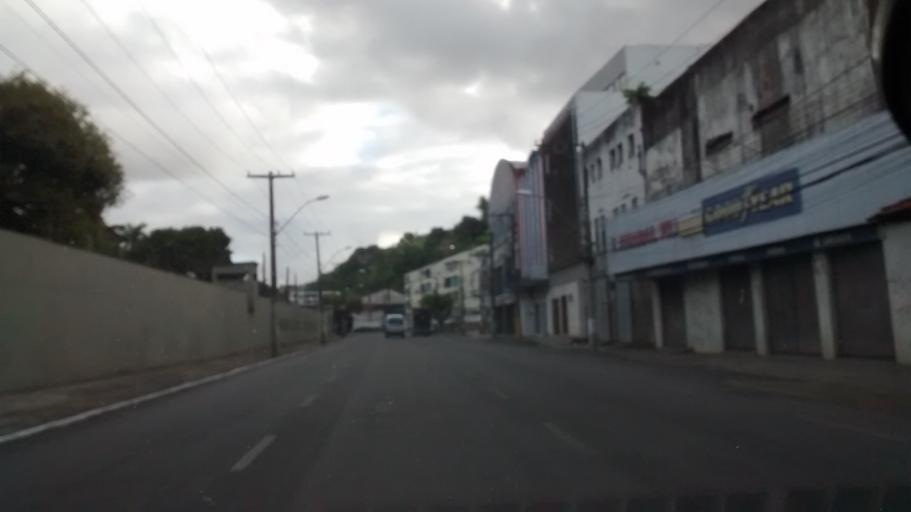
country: BR
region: Bahia
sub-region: Salvador
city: Salvador
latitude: -12.9656
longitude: -38.5071
